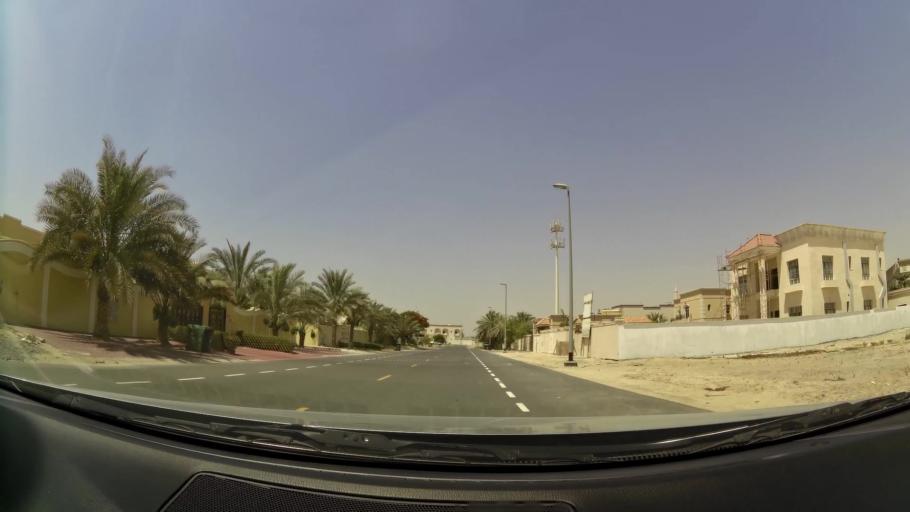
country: AE
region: Dubai
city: Dubai
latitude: 25.1071
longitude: 55.2188
